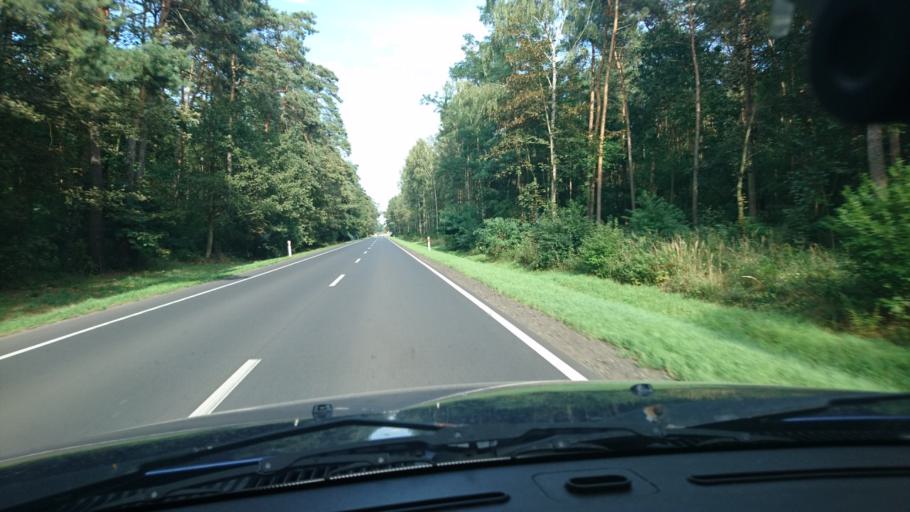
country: PL
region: Greater Poland Voivodeship
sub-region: Powiat krotoszynski
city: Kobylin
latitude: 51.7088
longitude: 17.1950
